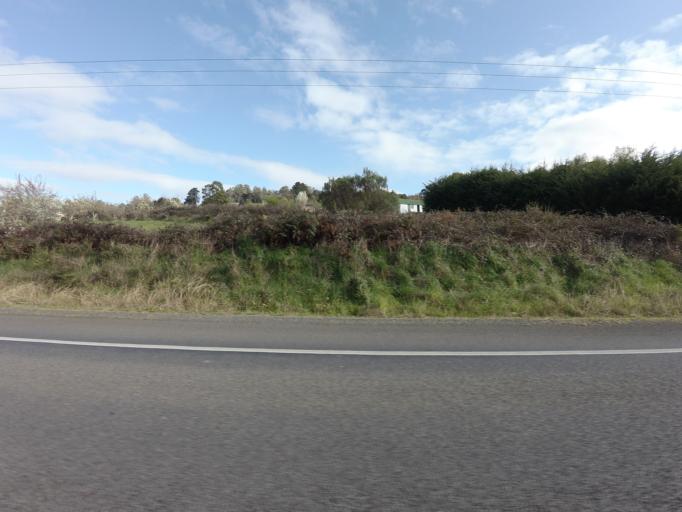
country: AU
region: Tasmania
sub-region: Huon Valley
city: Franklin
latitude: -43.1111
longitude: 146.9980
